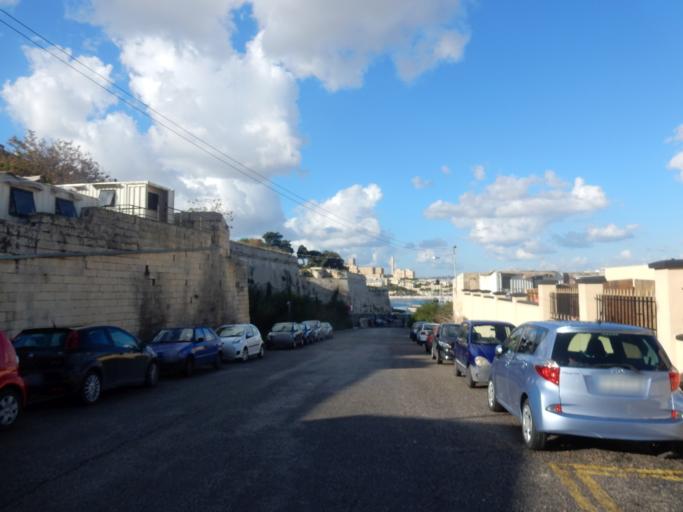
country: MT
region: Il-Furjana
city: Floriana
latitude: 35.8971
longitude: 14.5047
